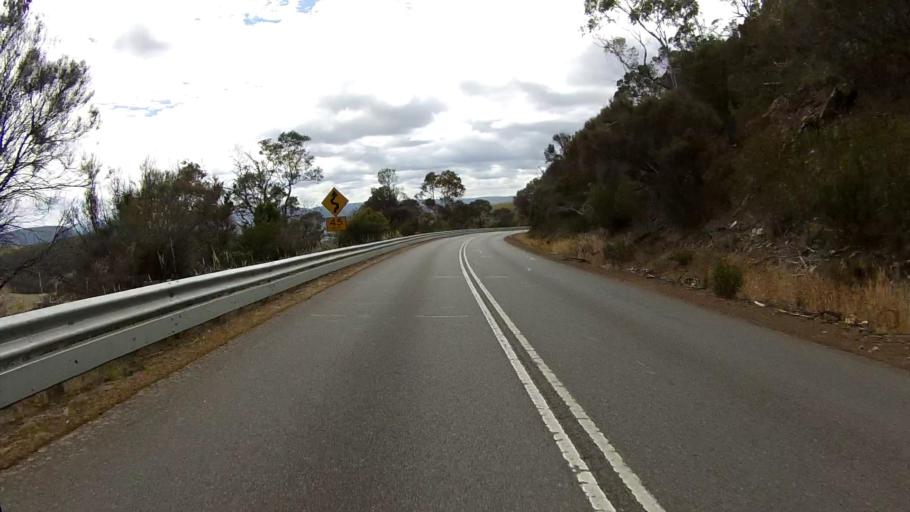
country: AU
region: Tasmania
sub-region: Clarence
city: Lindisfarne
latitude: -42.7795
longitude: 147.3673
